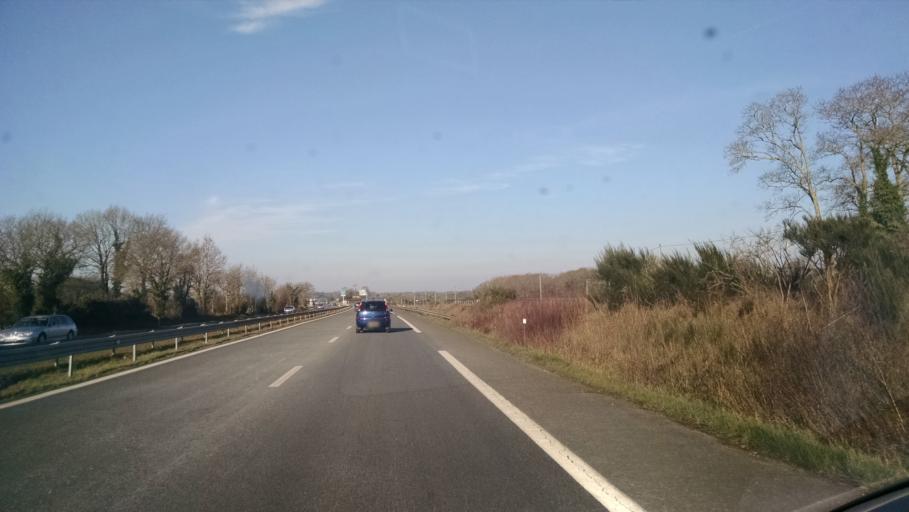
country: FR
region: Brittany
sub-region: Departement du Morbihan
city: Ambon
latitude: 47.5858
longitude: -2.5422
